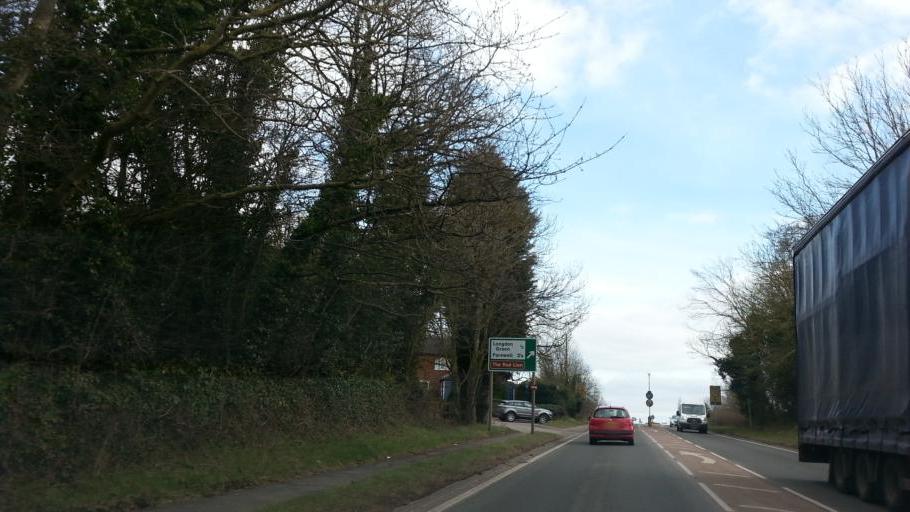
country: GB
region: England
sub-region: Staffordshire
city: Armitage
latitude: 52.7247
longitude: -1.8812
